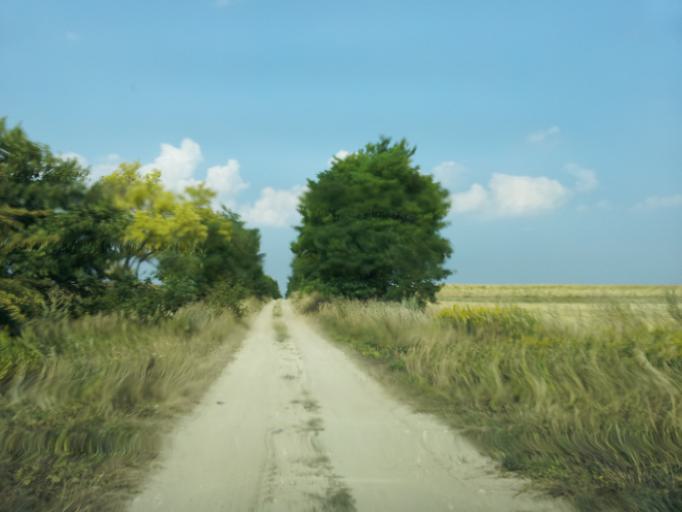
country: HU
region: Gyor-Moson-Sopron
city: Toltestava
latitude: 47.6164
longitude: 17.7141
